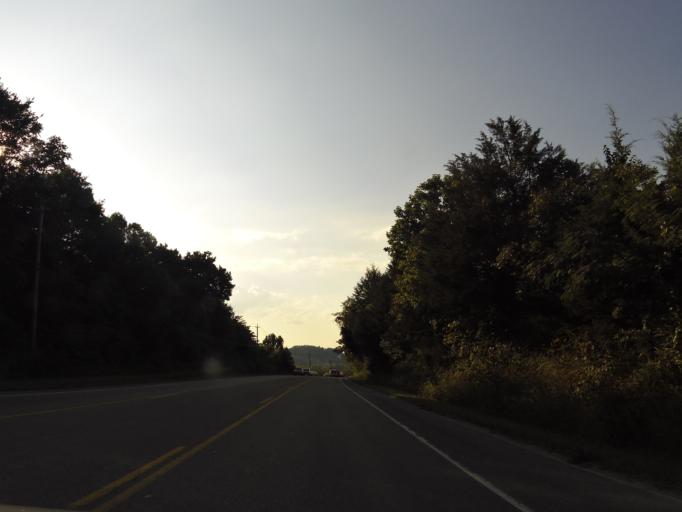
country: US
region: Tennessee
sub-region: Knox County
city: Knoxville
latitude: 35.9553
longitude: -83.8145
